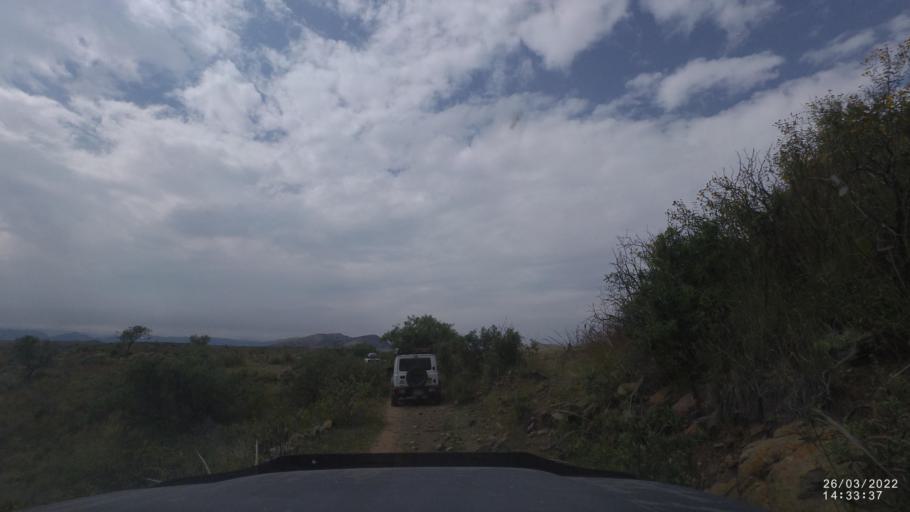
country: BO
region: Cochabamba
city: Cliza
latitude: -17.7417
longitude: -65.8676
